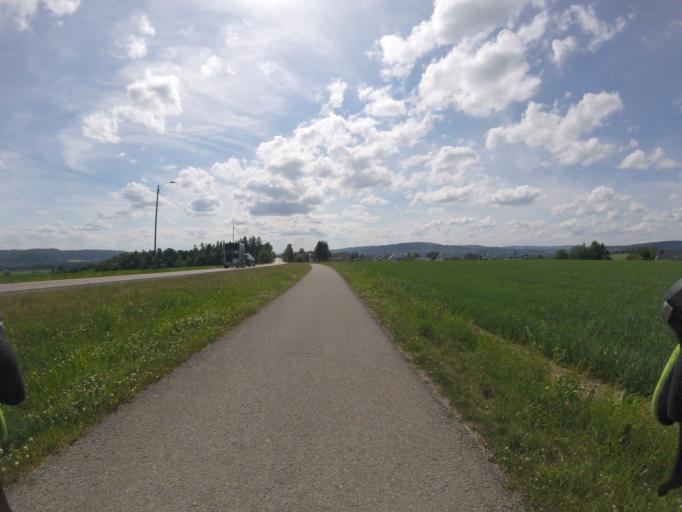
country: NO
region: Akershus
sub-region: Skedsmo
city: Lillestrom
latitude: 59.9864
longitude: 11.0481
